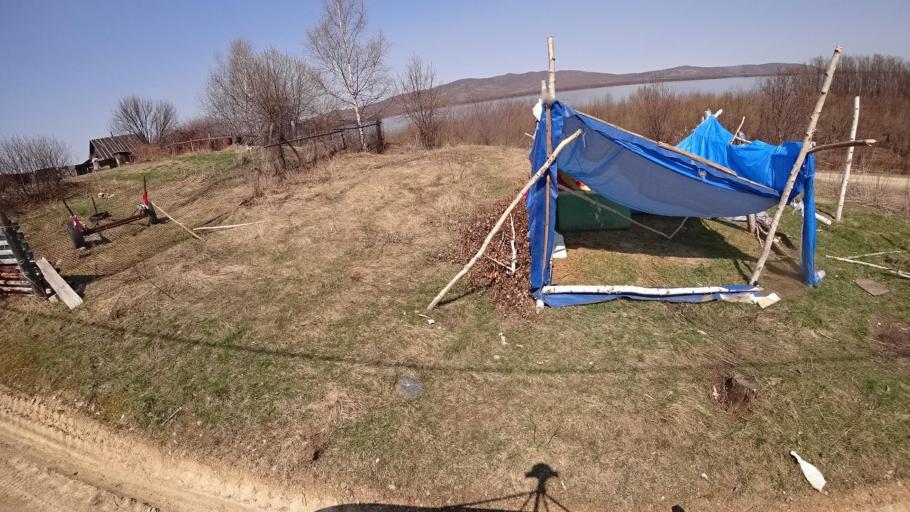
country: RU
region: Khabarovsk Krai
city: Selikhino
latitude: 50.6679
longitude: 137.4034
